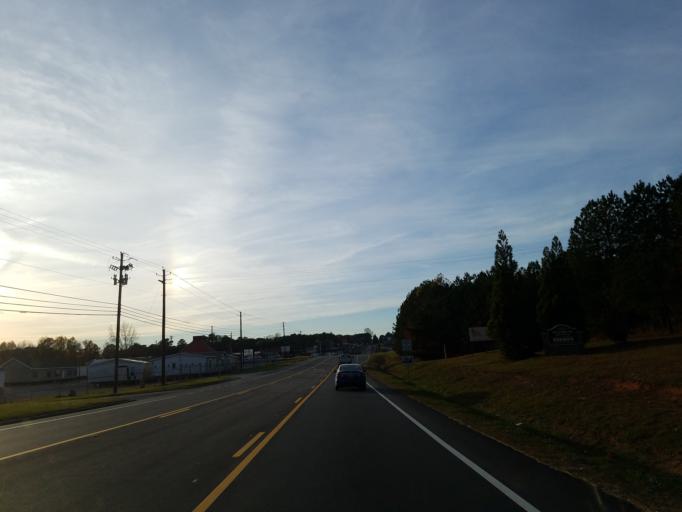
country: US
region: Georgia
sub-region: Haralson County
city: Bremen
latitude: 33.7219
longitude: -85.1204
